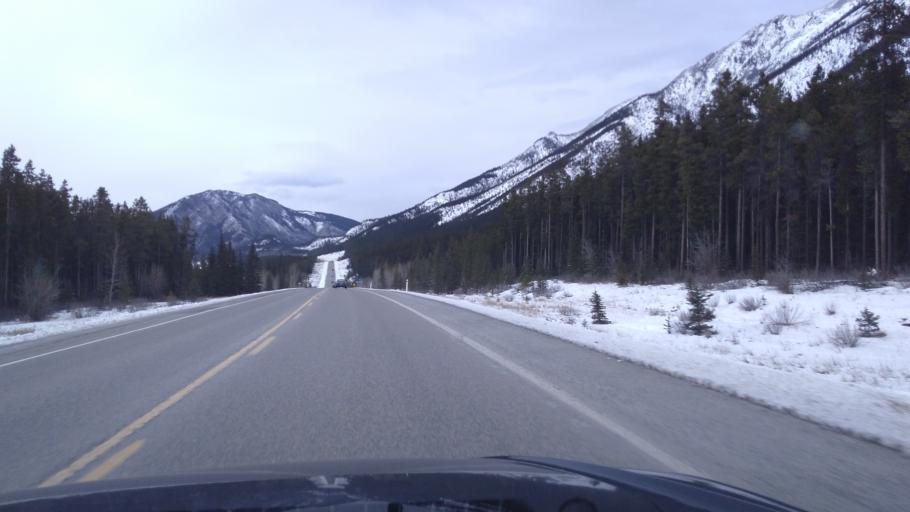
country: CA
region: Alberta
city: Canmore
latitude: 50.9851
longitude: -115.0752
